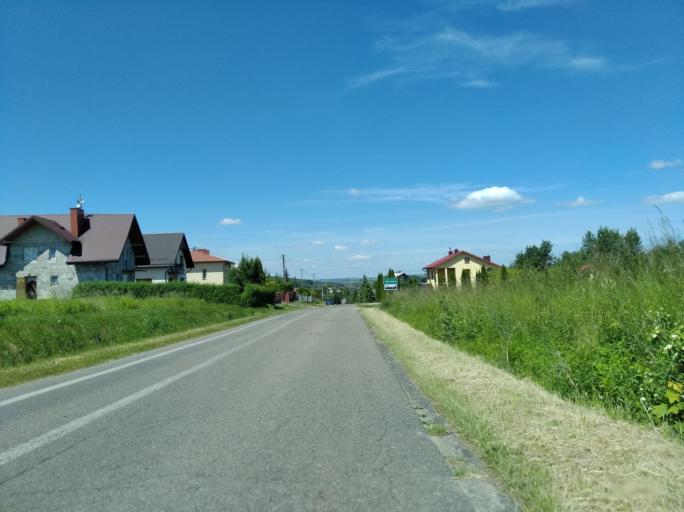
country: PL
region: Subcarpathian Voivodeship
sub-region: Powiat krosnienski
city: Chorkowka
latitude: 49.6423
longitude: 21.6176
